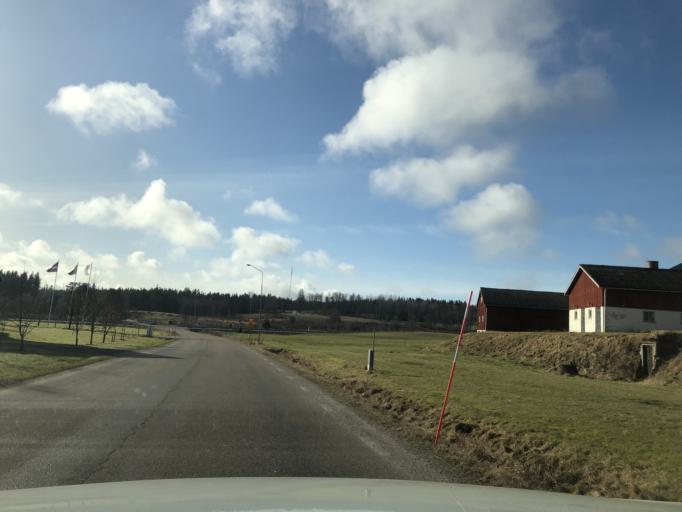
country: SE
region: Vaestra Goetaland
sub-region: Ulricehamns Kommun
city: Ulricehamn
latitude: 57.7990
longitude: 13.5956
